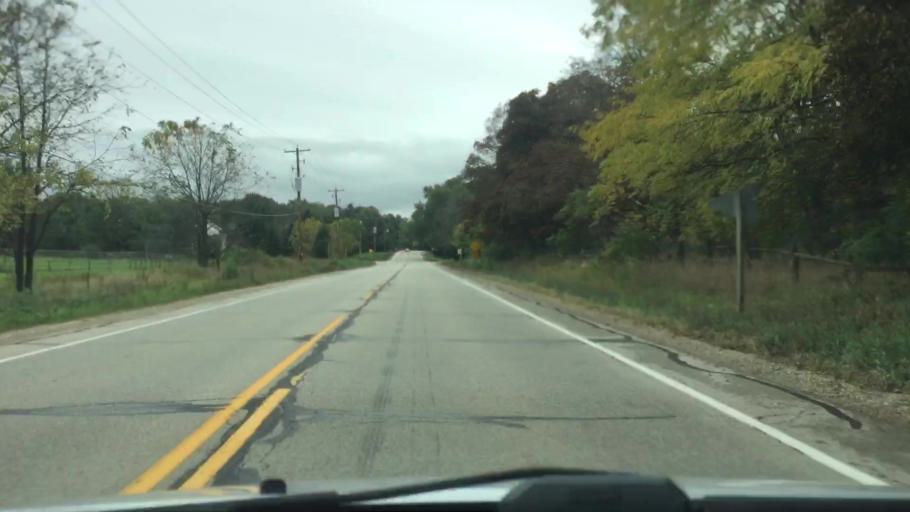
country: US
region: Wisconsin
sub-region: Walworth County
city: Elkhorn
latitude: 42.7726
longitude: -88.5550
